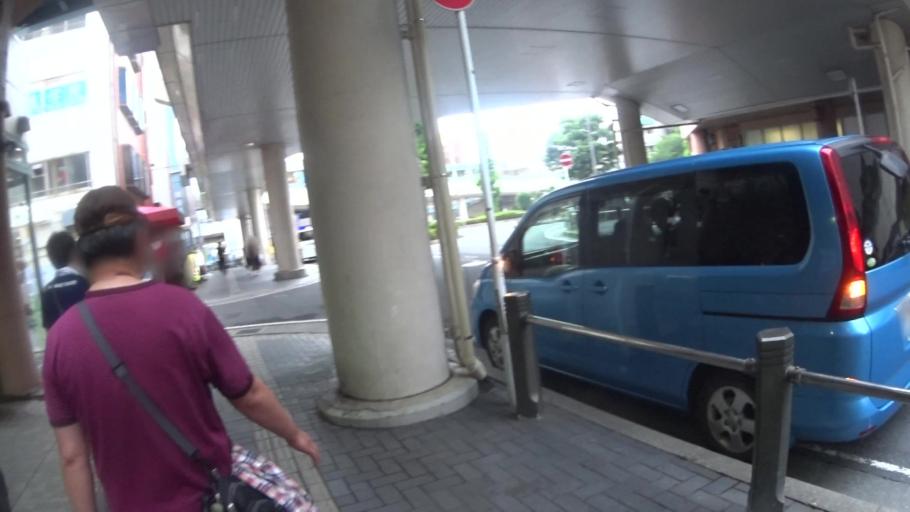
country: JP
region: Chiba
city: Nagareyama
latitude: 35.8326
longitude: 139.9313
